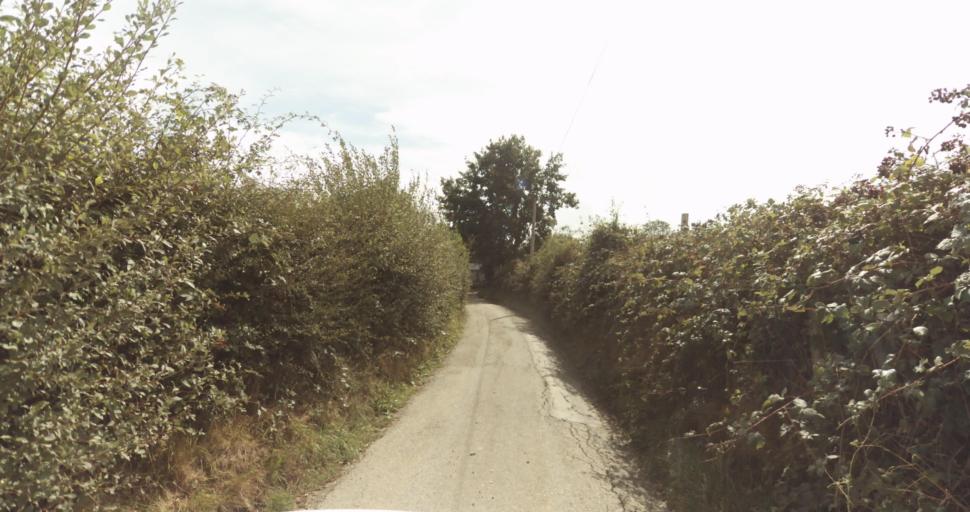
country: FR
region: Lower Normandy
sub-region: Departement de l'Orne
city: Sainte-Gauburge-Sainte-Colombe
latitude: 48.7969
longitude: 0.3986
